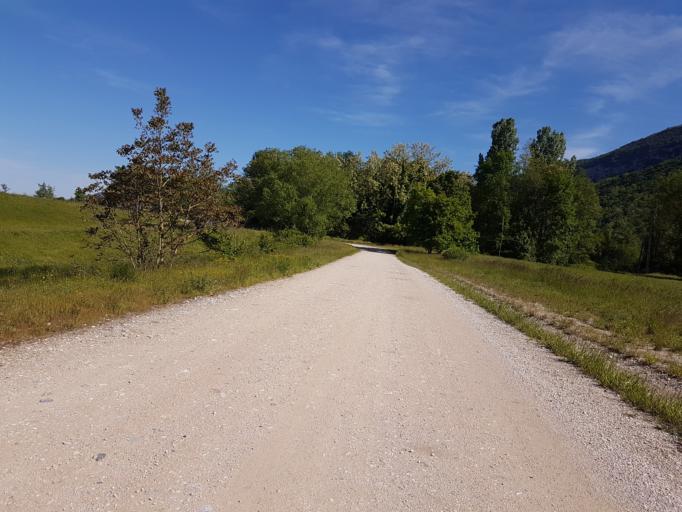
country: FR
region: Rhone-Alpes
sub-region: Departement de l'Ain
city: Villebois
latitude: 45.8267
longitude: 5.4382
